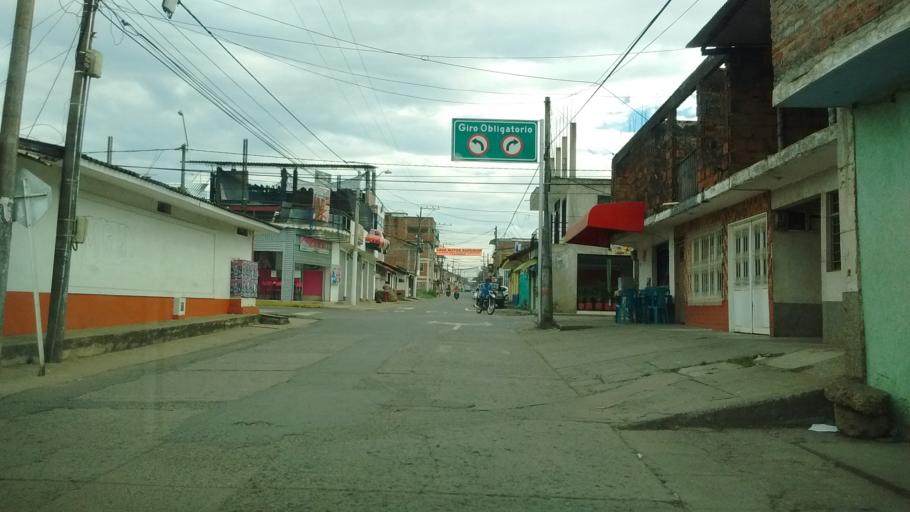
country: CO
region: Cauca
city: Santander de Quilichao
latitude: 3.0158
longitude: -76.4809
